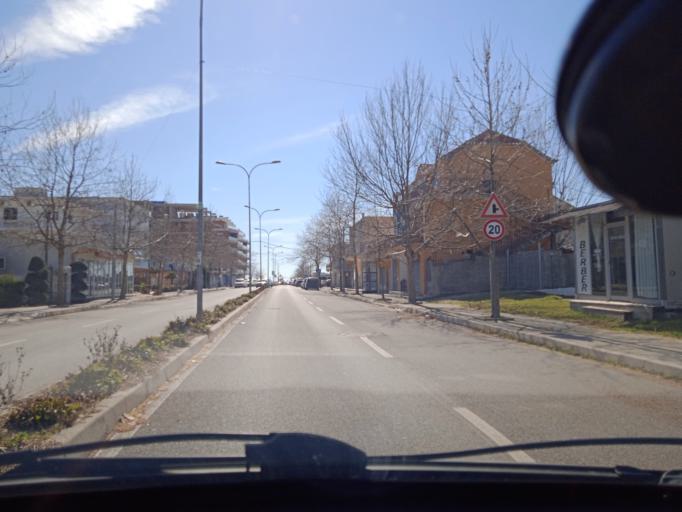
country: AL
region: Shkoder
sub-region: Rrethi i Shkodres
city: Velipoje
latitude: 41.8648
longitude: 19.4260
